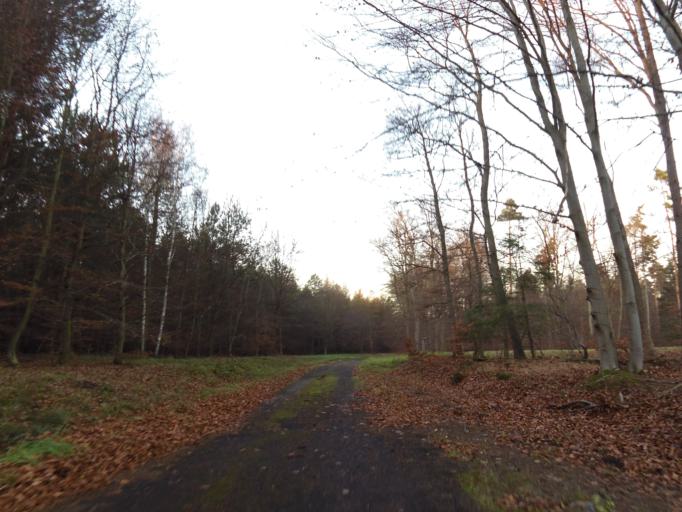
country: DE
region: Hesse
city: Morfelden-Walldorf
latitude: 49.9976
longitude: 8.6073
